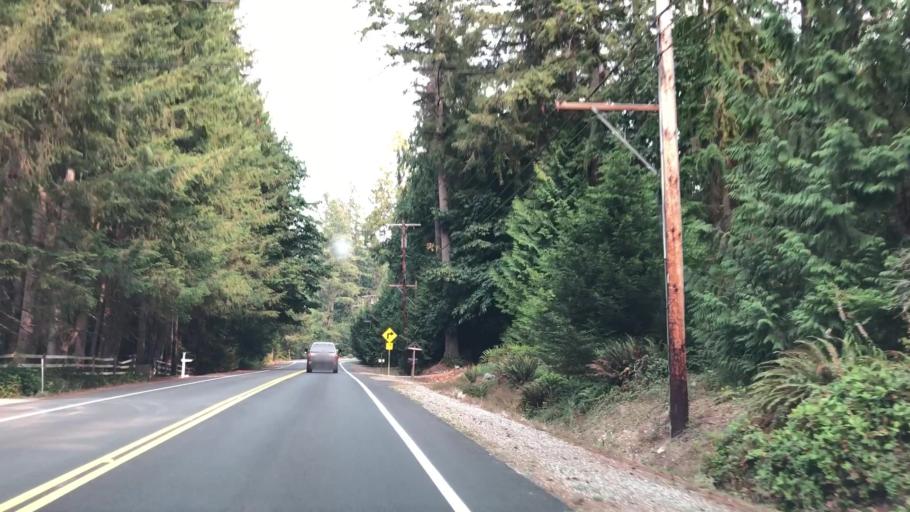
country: US
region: Washington
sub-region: King County
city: Cottage Lake
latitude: 47.7477
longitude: -122.0510
